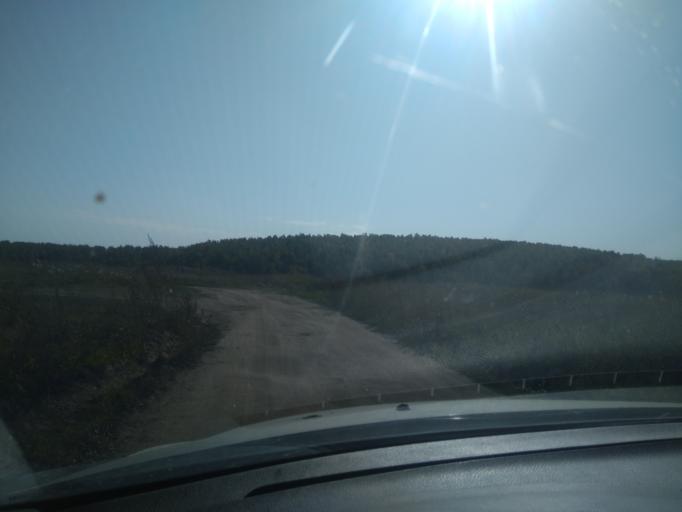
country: RU
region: Sverdlovsk
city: Pokrovskoye
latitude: 56.4359
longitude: 61.6016
